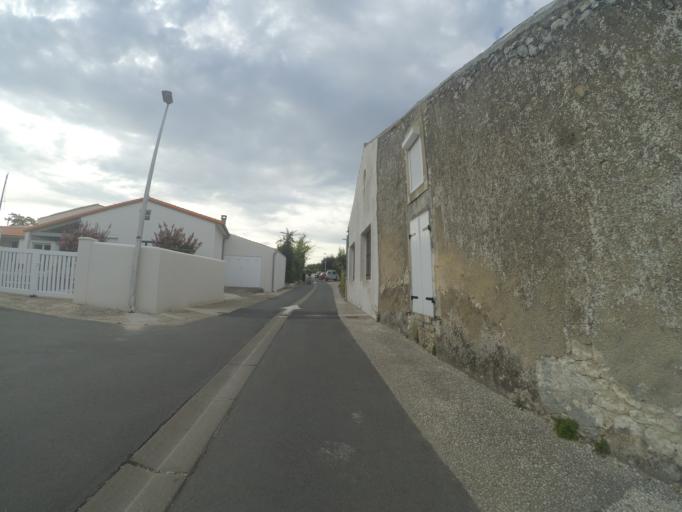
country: FR
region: Poitou-Charentes
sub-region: Departement de la Charente-Maritime
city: Meschers-sur-Gironde
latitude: 45.5577
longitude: -0.9548
